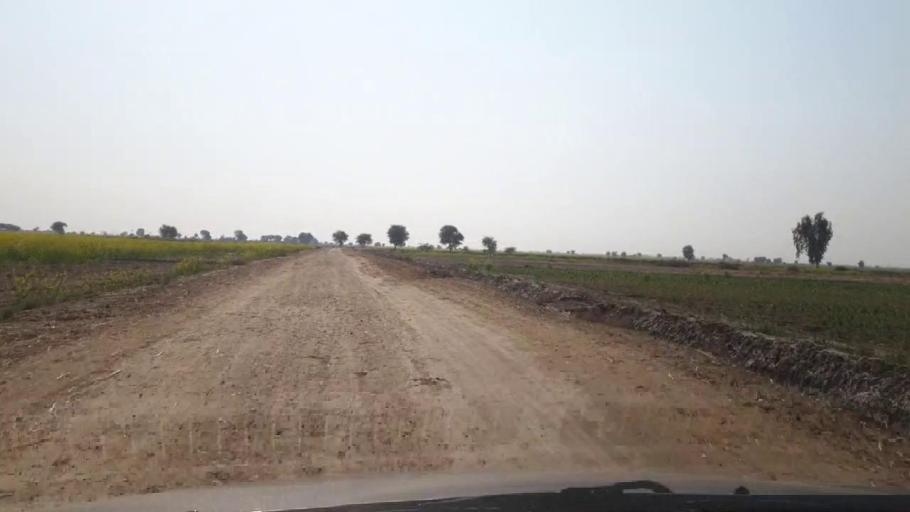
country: PK
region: Sindh
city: Jhol
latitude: 25.8630
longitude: 68.9982
